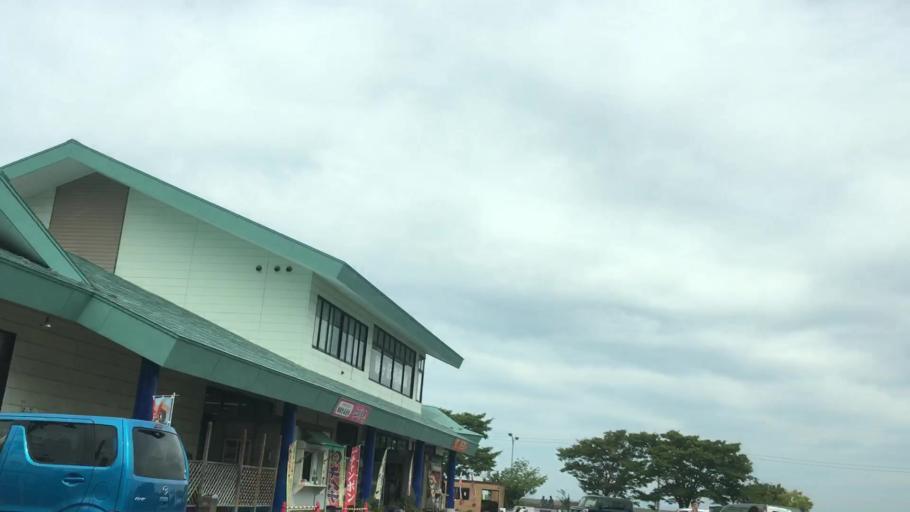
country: JP
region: Aomori
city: Shimokizukuri
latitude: 40.7788
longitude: 140.2103
